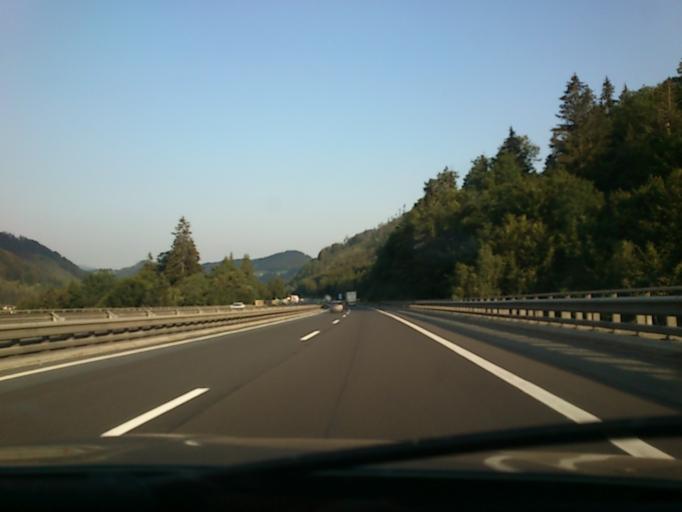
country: AT
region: Styria
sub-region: Politischer Bezirk Graz-Umgebung
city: Ubelbach
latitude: 47.2302
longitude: 15.2165
